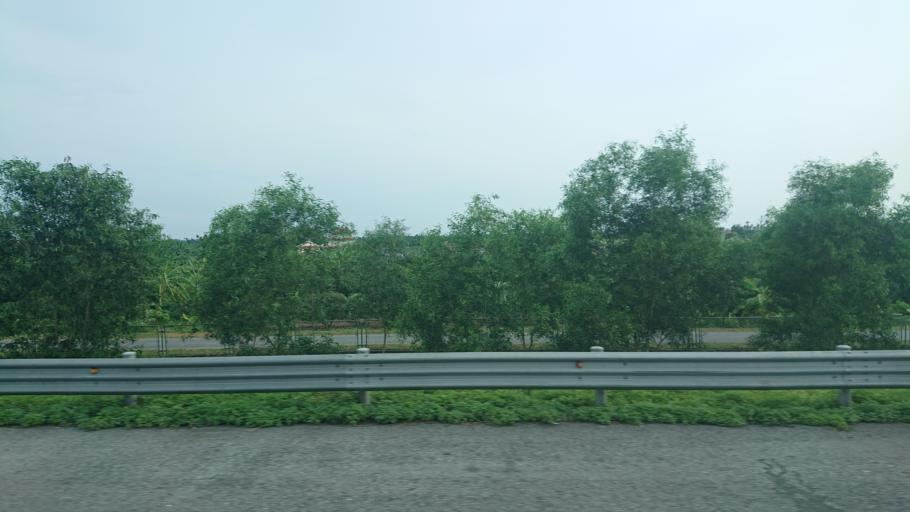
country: VN
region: Hai Duong
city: Tu Ky
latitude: 20.8296
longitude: 106.4513
